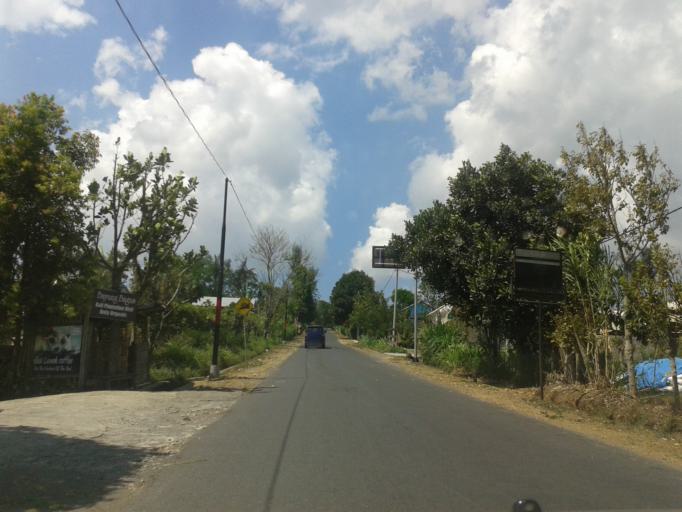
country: ID
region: Bali
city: Banjar Kedisan
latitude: -8.2941
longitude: 115.3402
